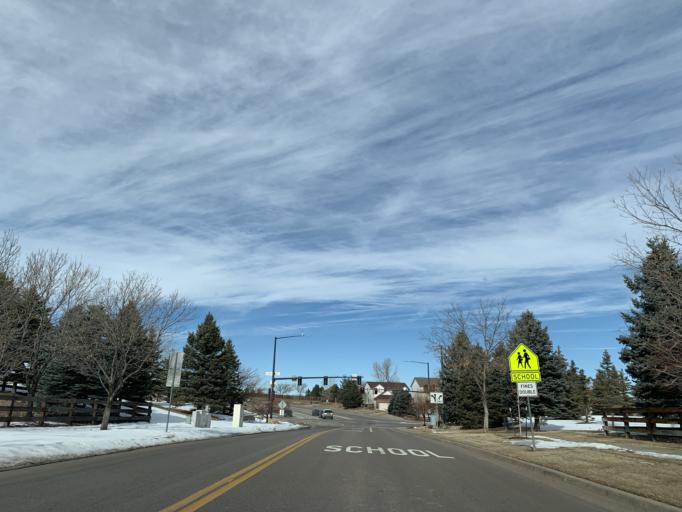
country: US
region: Colorado
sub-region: Douglas County
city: Carriage Club
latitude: 39.5206
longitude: -104.9167
